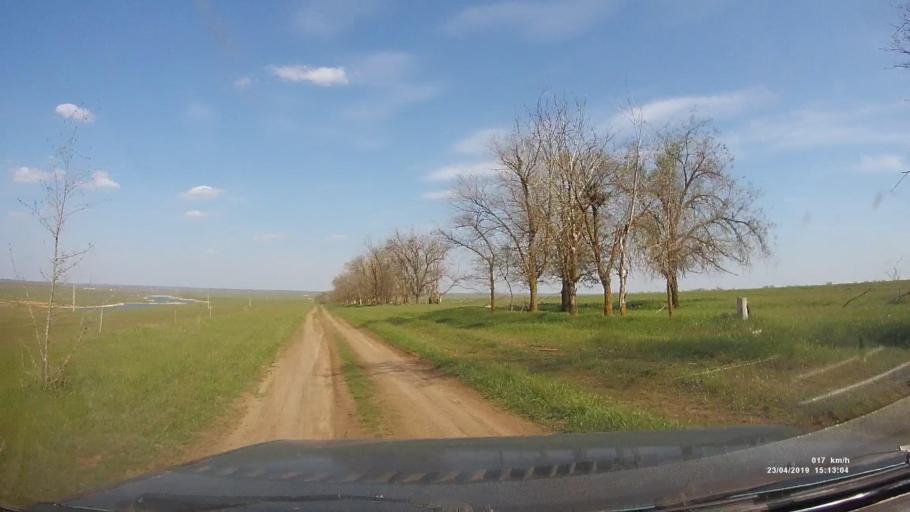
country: RU
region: Rostov
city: Remontnoye
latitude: 46.5399
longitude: 42.9537
